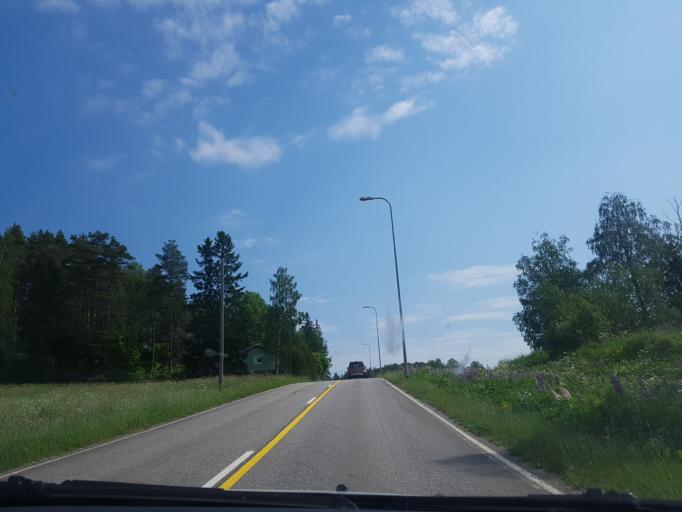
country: FI
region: Uusimaa
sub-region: Helsinki
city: Vihti
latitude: 60.3287
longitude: 24.4159
